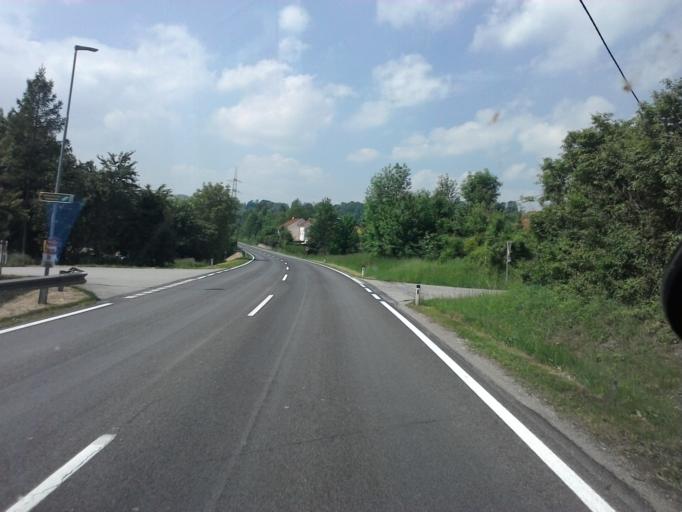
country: AT
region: Upper Austria
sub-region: Politischer Bezirk Steyr-Land
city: Sierning
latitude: 48.0522
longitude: 14.3621
